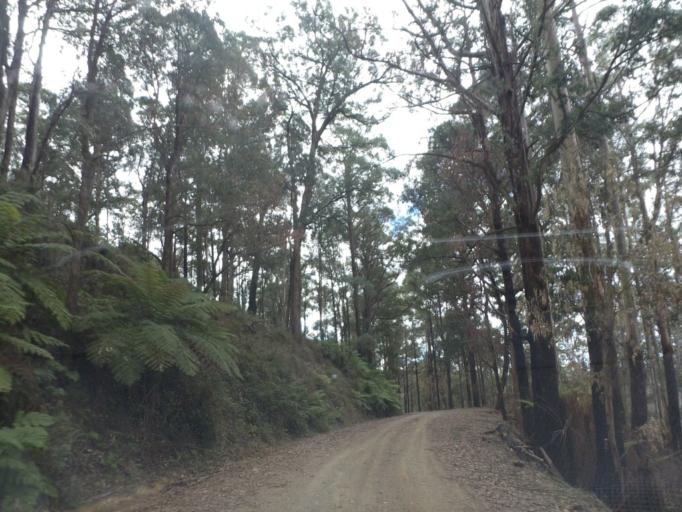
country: AU
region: Victoria
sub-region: Murrindindi
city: Alexandra
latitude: -37.4551
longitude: 145.9667
